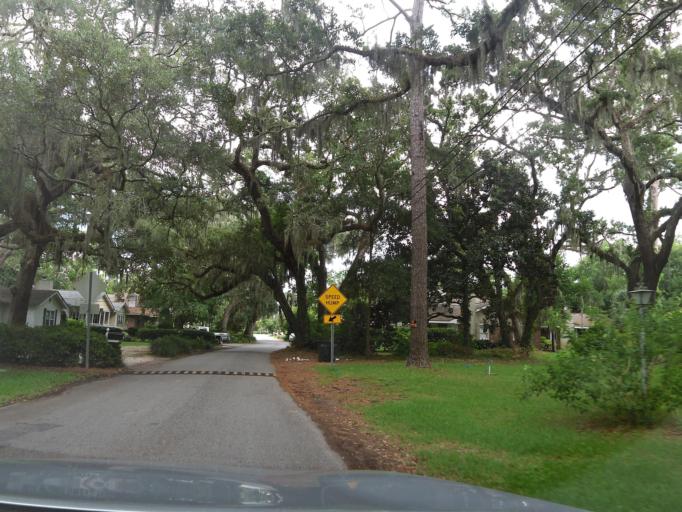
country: US
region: Georgia
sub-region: Glynn County
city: Saint Simons Island
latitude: 31.1375
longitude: -81.3915
